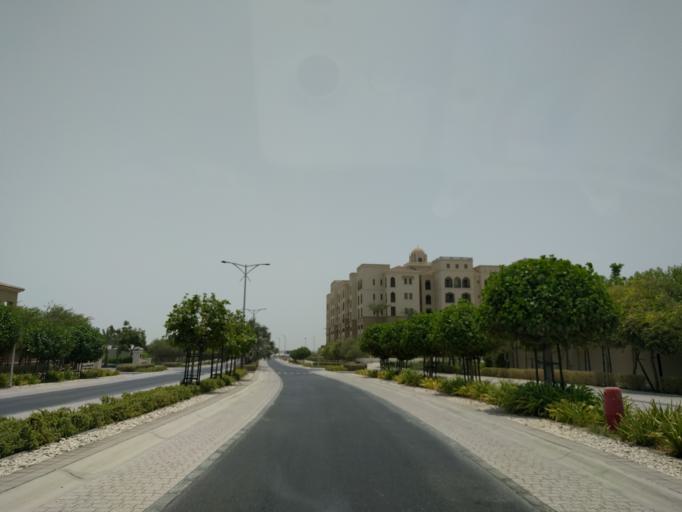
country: AE
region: Abu Dhabi
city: Abu Dhabi
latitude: 24.5531
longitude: 54.4500
